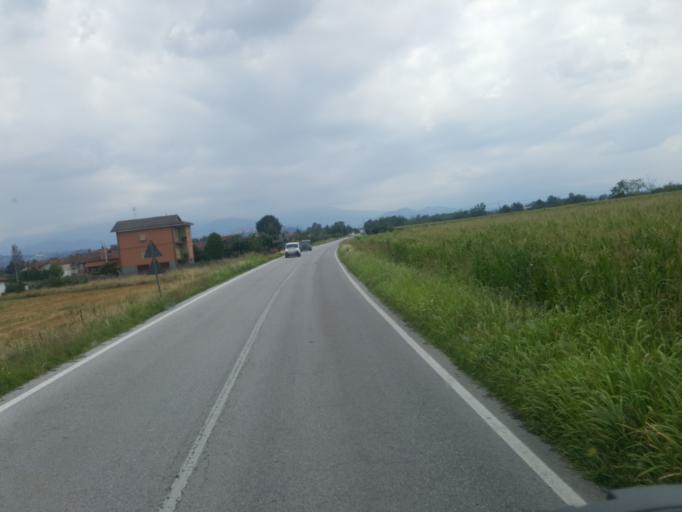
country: IT
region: Piedmont
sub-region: Provincia di Cuneo
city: Bastia Mondovi
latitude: 44.4386
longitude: 7.8689
